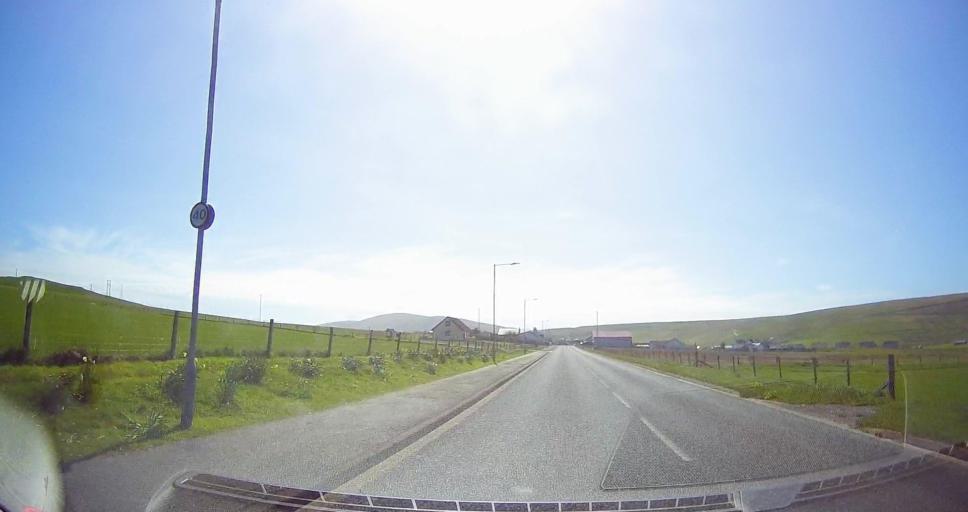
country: GB
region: Scotland
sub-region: Shetland Islands
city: Sandwick
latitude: 60.0018
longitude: -1.2375
